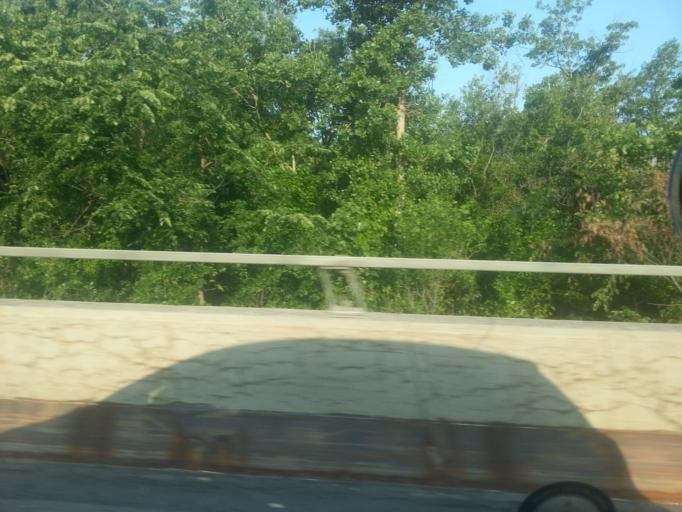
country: CA
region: Quebec
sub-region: Outaouais
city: Gatineau
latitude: 45.4557
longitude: -75.7163
